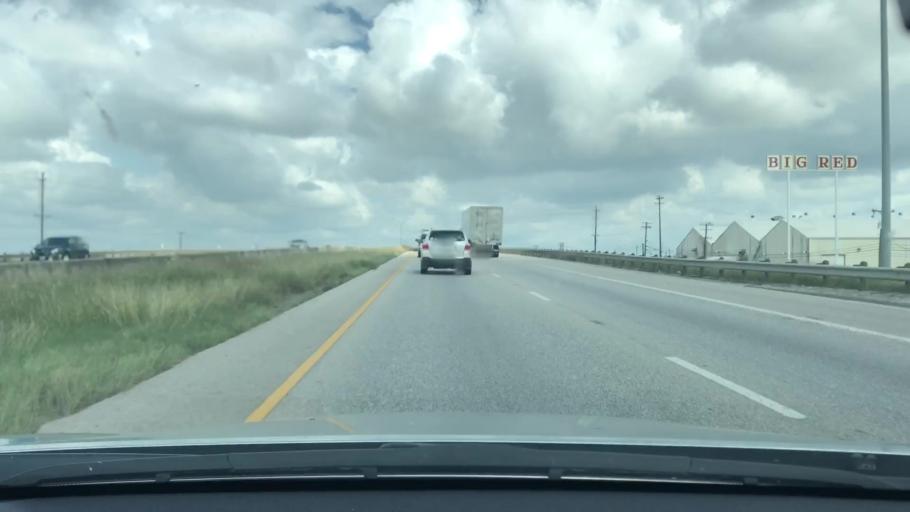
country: US
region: Texas
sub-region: Bexar County
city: Kirby
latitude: 29.4580
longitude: -98.4041
